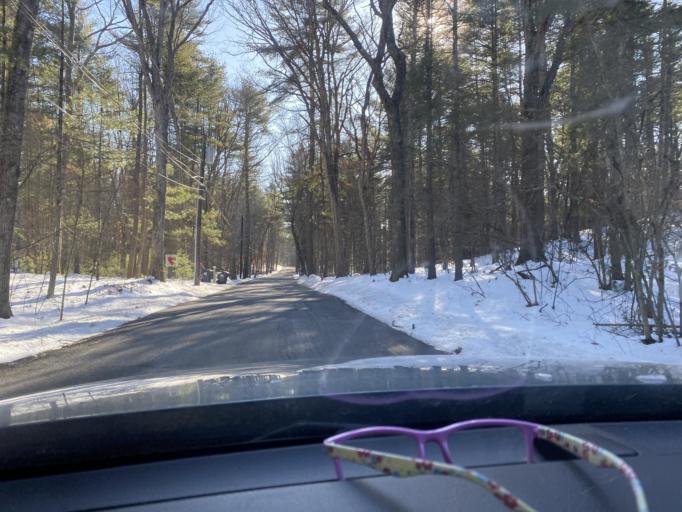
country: US
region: Massachusetts
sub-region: Norfolk County
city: Medfield
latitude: 42.1809
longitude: -71.2816
